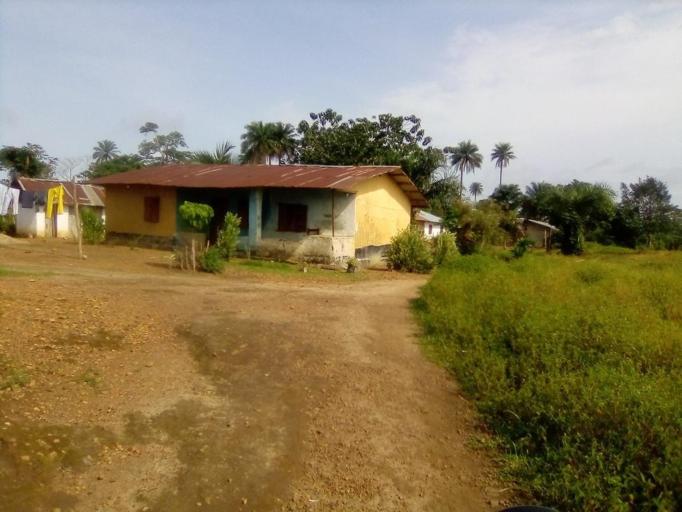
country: SL
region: Southern Province
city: Pujehun
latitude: 7.3649
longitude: -11.7283
